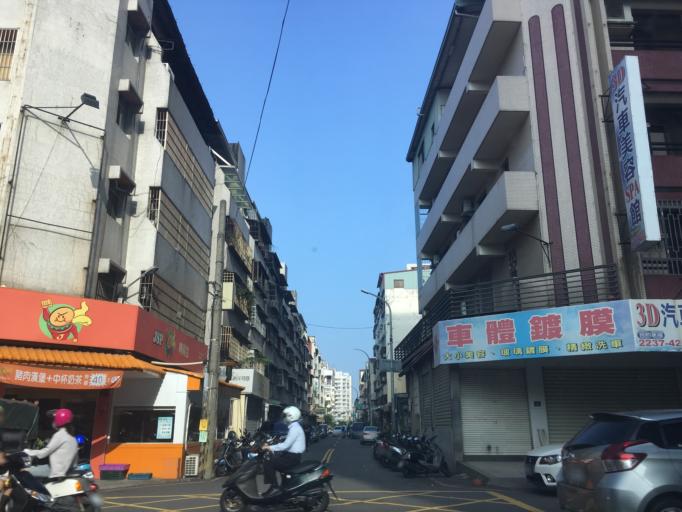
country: TW
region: Taiwan
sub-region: Taichung City
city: Taichung
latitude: 24.1716
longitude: 120.6836
